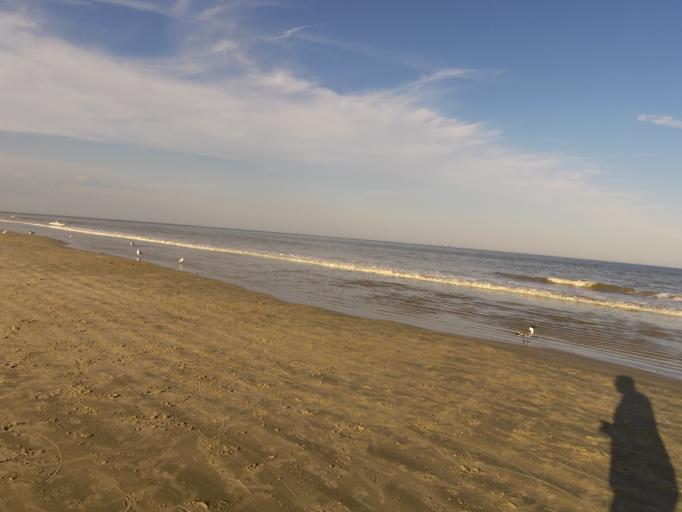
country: US
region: Florida
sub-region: Duval County
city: Atlantic Beach
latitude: 30.3672
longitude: -81.3972
